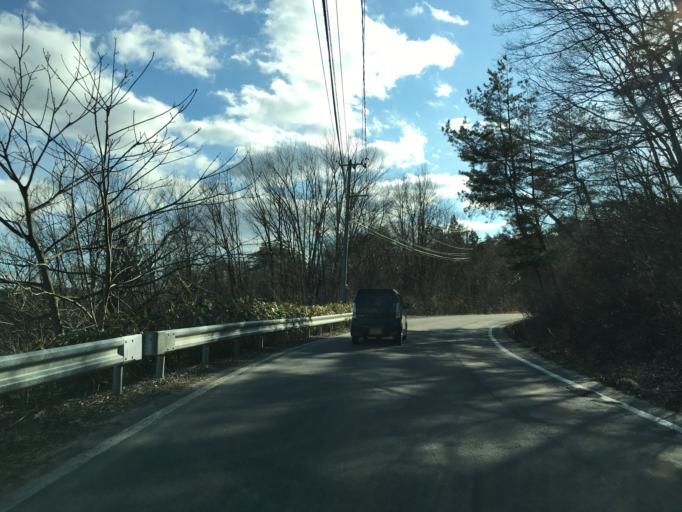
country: JP
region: Yamagata
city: Nagai
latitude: 37.9852
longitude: 140.0030
